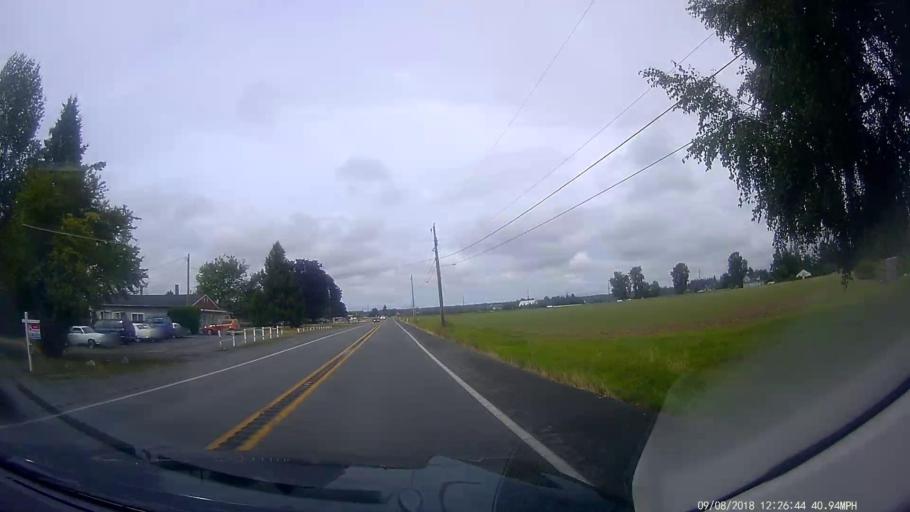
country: US
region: Washington
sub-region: Skagit County
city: Mount Vernon
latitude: 48.4389
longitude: -122.3835
